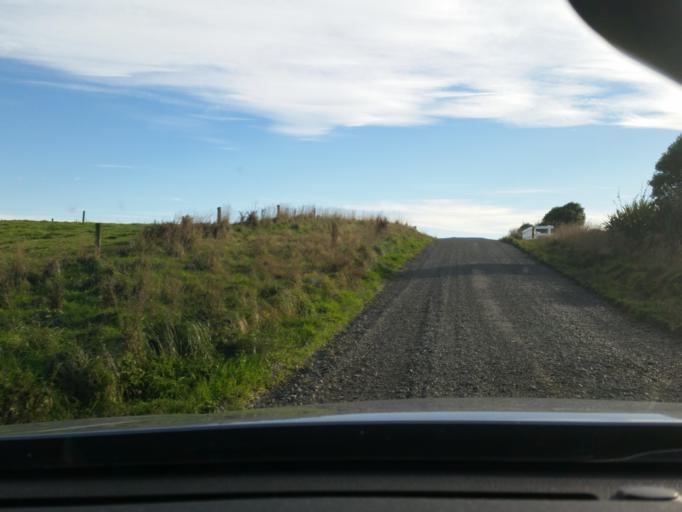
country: NZ
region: Southland
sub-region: Southland District
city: Riverton
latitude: -46.2699
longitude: 168.0247
